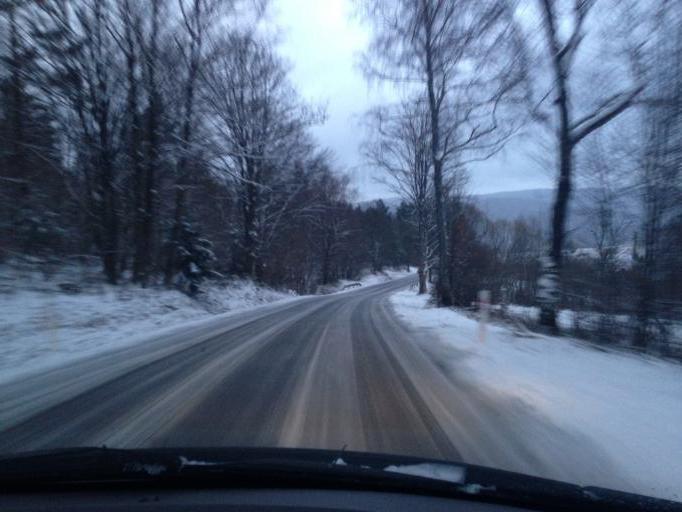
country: PL
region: Subcarpathian Voivodeship
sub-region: Powiat jasielski
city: Krempna
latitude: 49.5254
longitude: 21.5017
